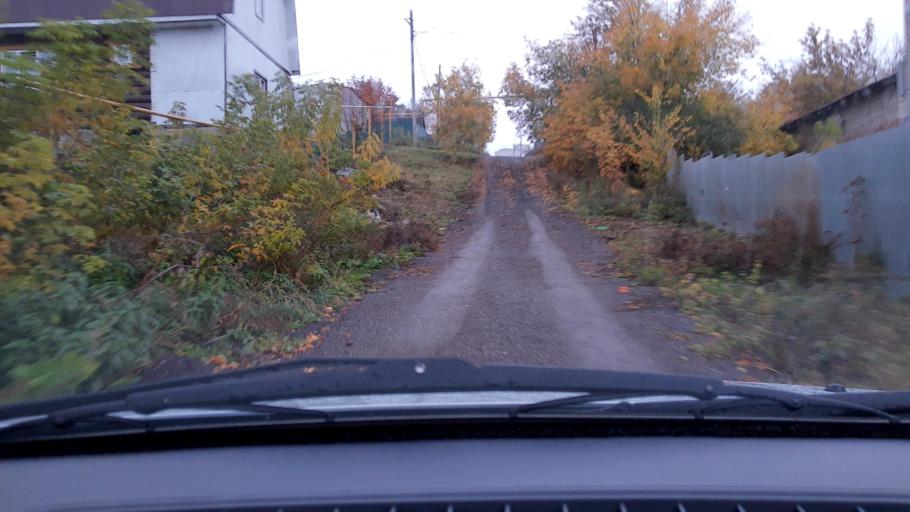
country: RU
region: Bashkortostan
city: Ufa
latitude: 54.7802
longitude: 56.0450
